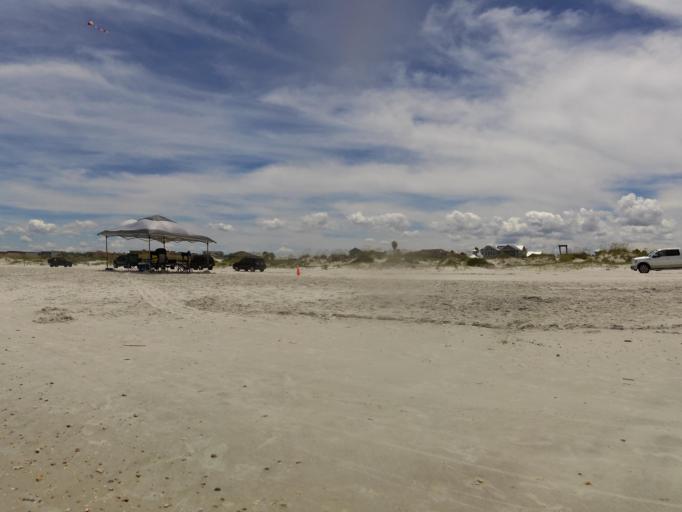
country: US
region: Florida
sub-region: Saint Johns County
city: Saint Augustine Beach
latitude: 29.8262
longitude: -81.2626
